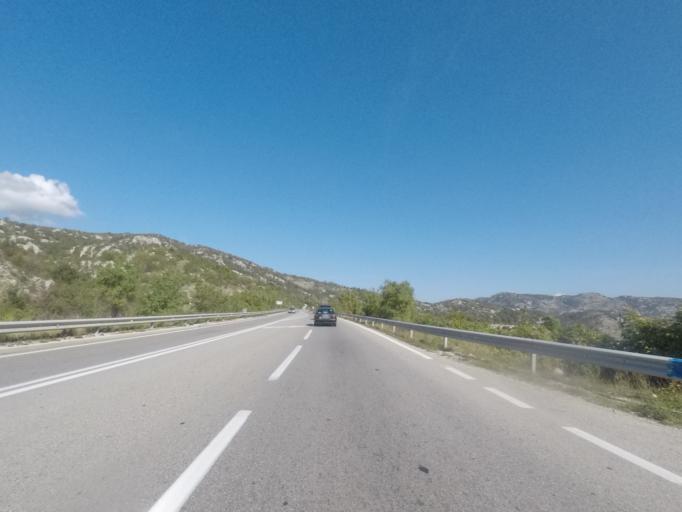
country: ME
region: Opstina Niksic
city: Niksic
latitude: 42.6870
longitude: 18.9628
